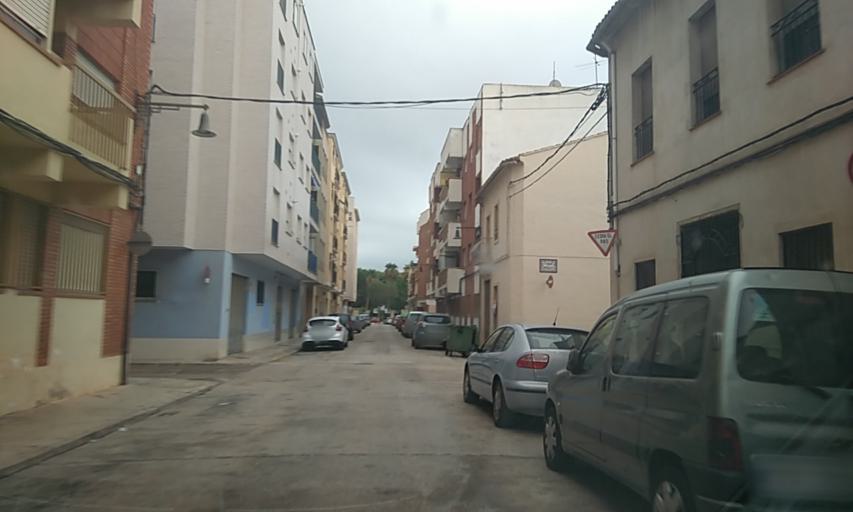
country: ES
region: Valencia
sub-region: Provincia de Valencia
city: L'Alcudia
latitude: 39.1923
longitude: -0.5091
